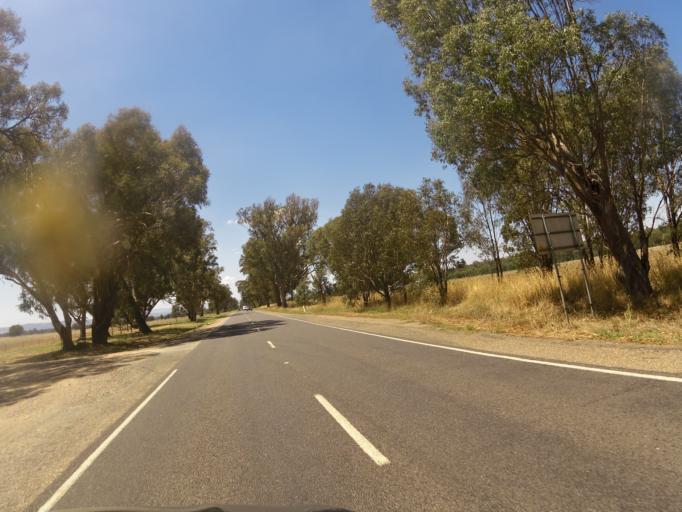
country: AU
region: Victoria
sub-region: Wangaratta
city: Wangaratta
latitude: -36.3819
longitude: 146.4060
